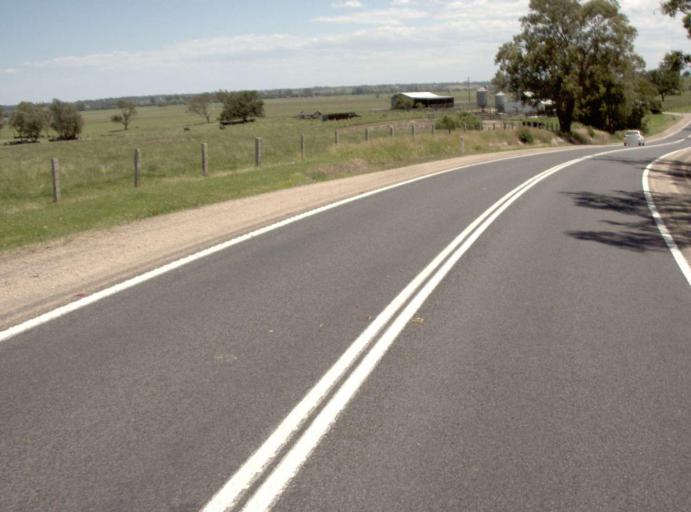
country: AU
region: Victoria
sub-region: East Gippsland
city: Lakes Entrance
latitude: -37.7054
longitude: 148.5129
